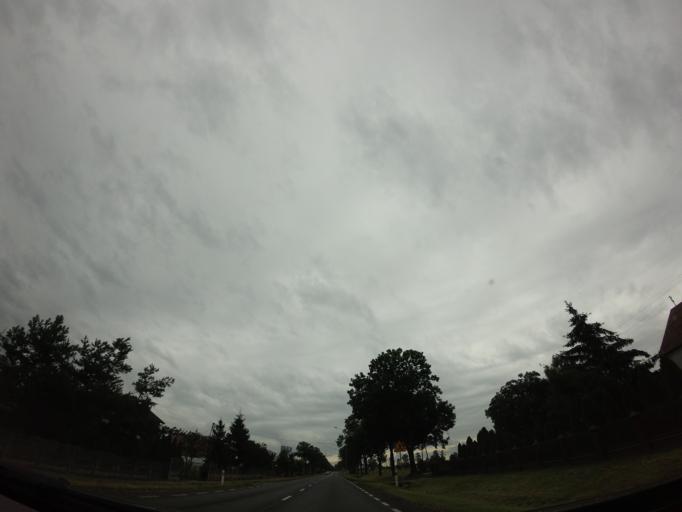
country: PL
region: Masovian Voivodeship
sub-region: Powiat plonski
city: Raciaz
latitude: 52.7746
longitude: 20.0885
